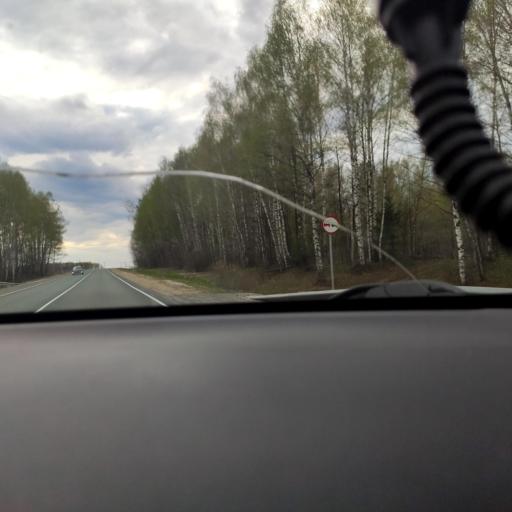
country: RU
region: Mariy-El
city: Krasnogorskiy
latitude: 56.1870
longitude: 48.2487
